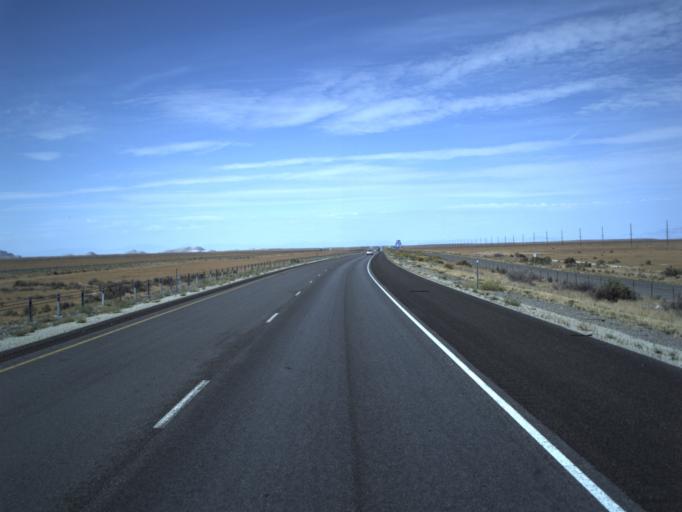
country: US
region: Utah
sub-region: Tooele County
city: Grantsville
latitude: 40.7260
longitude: -113.1433
